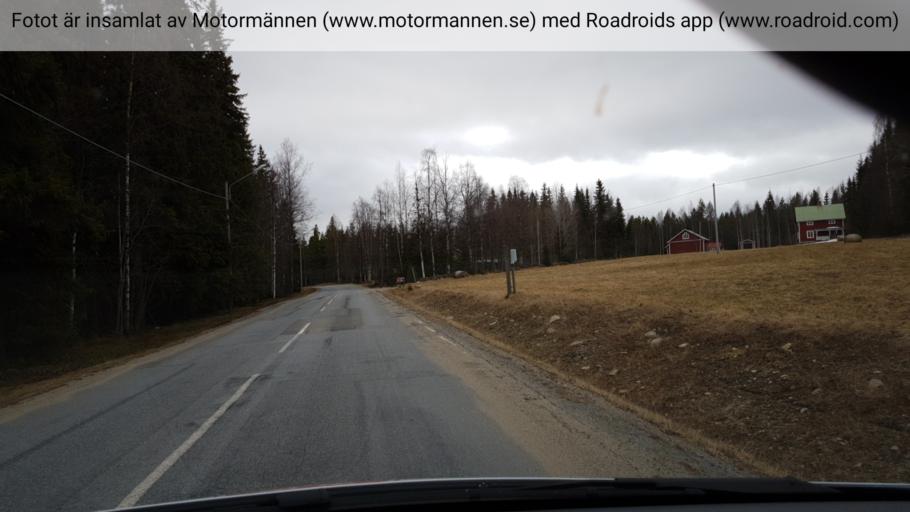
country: SE
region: Vaesterbotten
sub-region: Lycksele Kommun
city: Lycksele
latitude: 64.0636
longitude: 18.4003
